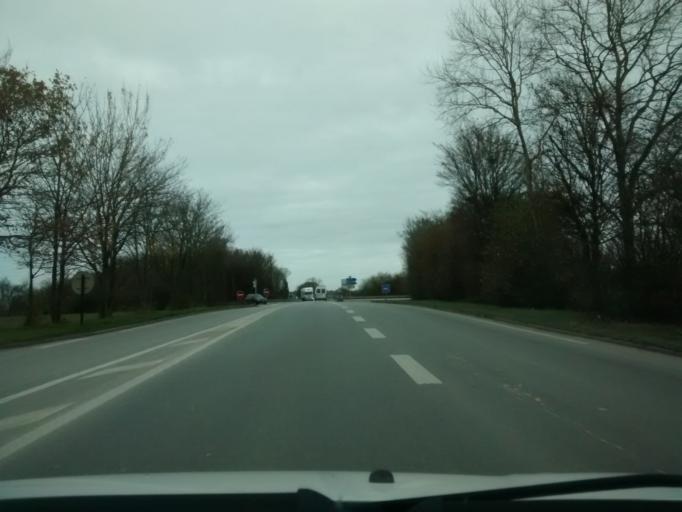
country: FR
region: Brittany
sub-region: Departement d'Ille-et-Vilaine
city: Etrelles
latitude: 48.0702
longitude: -1.1986
